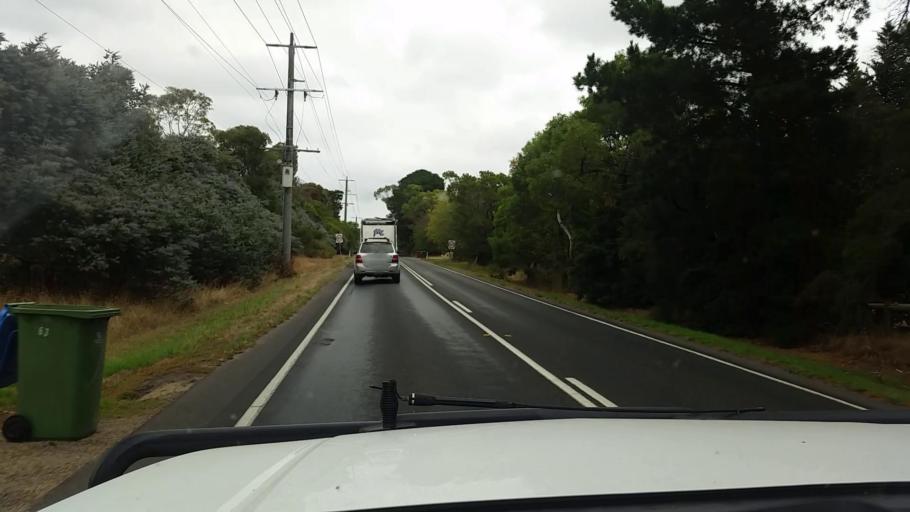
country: AU
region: Victoria
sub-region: Mornington Peninsula
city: Hastings
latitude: -38.2846
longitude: 145.1643
